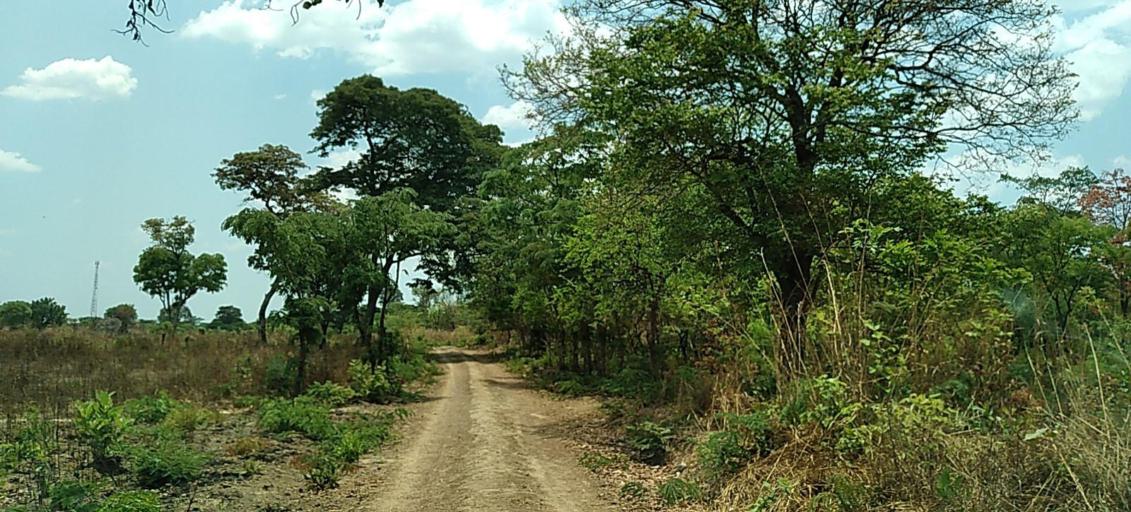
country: ZM
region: Copperbelt
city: Chililabombwe
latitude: -12.4532
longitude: 27.6751
